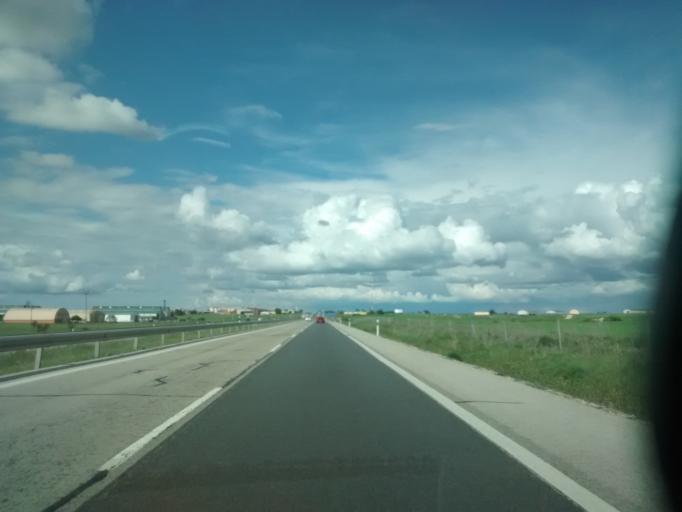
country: ES
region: Castille-La Mancha
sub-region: Provincia de Guadalajara
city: Trijueque
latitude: 40.7658
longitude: -3.0050
